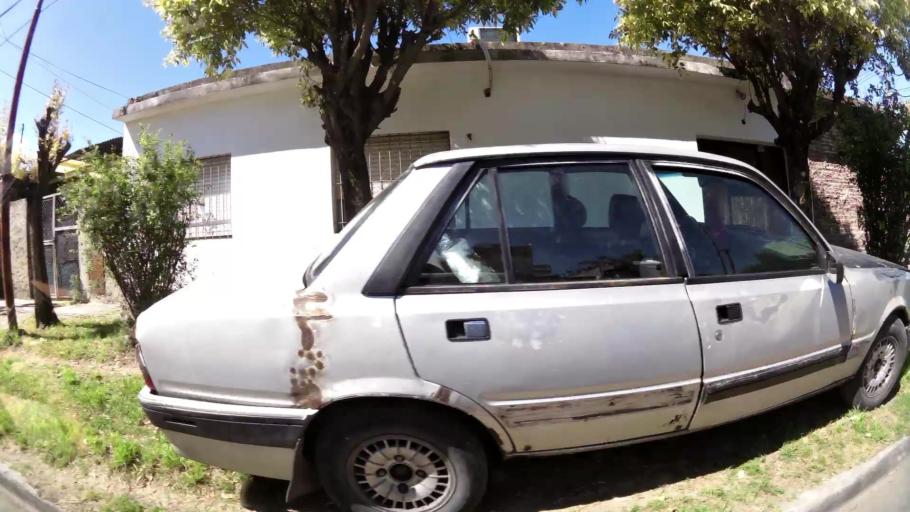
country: AR
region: Buenos Aires
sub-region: Partido de General San Martin
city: General San Martin
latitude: -34.5202
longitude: -58.5673
